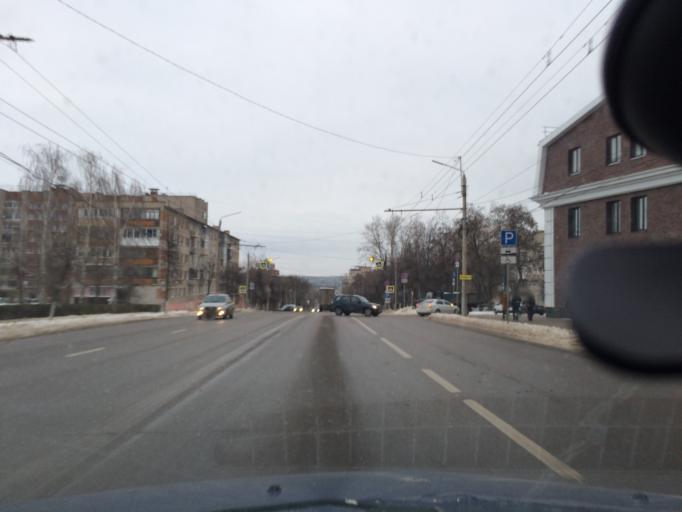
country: RU
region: Tula
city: Tula
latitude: 54.1918
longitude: 37.5840
